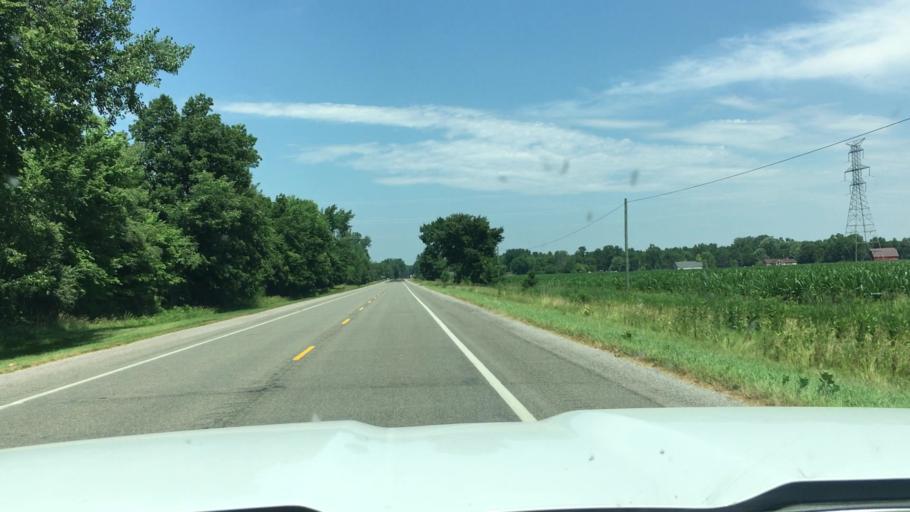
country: US
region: Michigan
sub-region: Saginaw County
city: Chesaning
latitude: 43.2089
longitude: -84.1694
